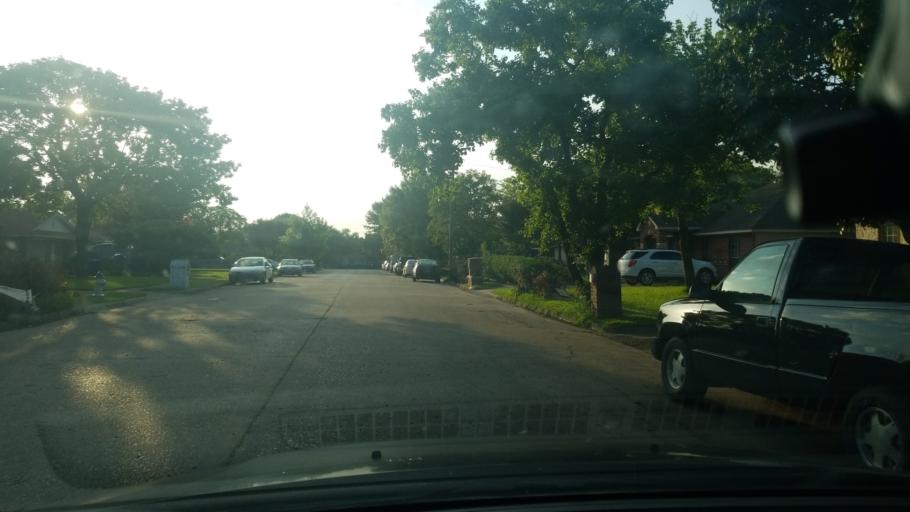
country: US
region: Texas
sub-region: Dallas County
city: Balch Springs
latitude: 32.7255
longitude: -96.6501
